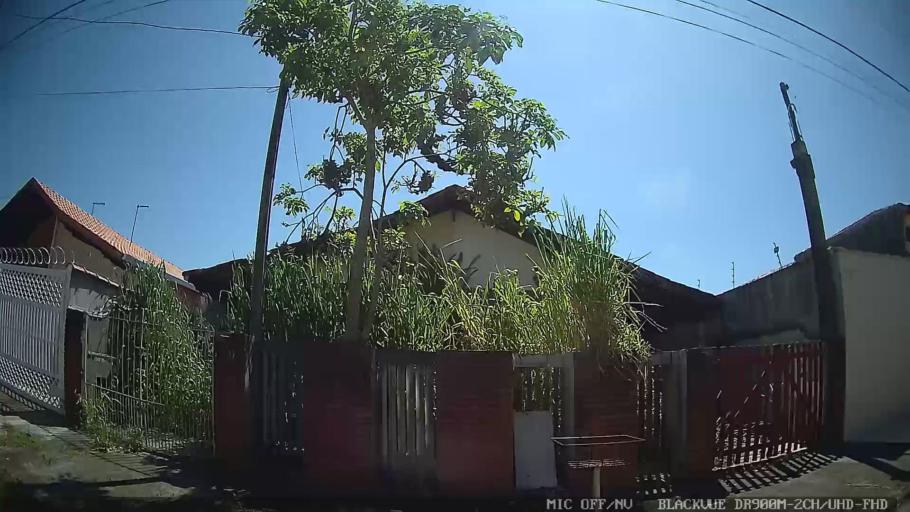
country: BR
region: Sao Paulo
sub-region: Peruibe
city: Peruibe
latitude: -24.2993
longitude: -46.9807
